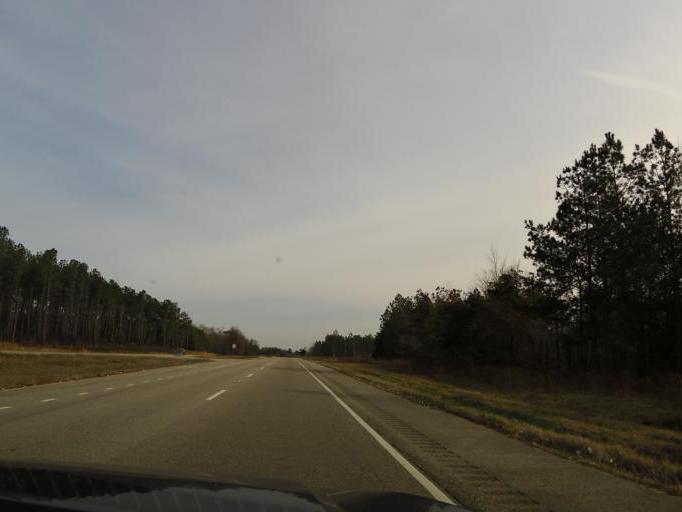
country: US
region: Alabama
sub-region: Houston County
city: Ashford
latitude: 31.1336
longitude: -85.1042
